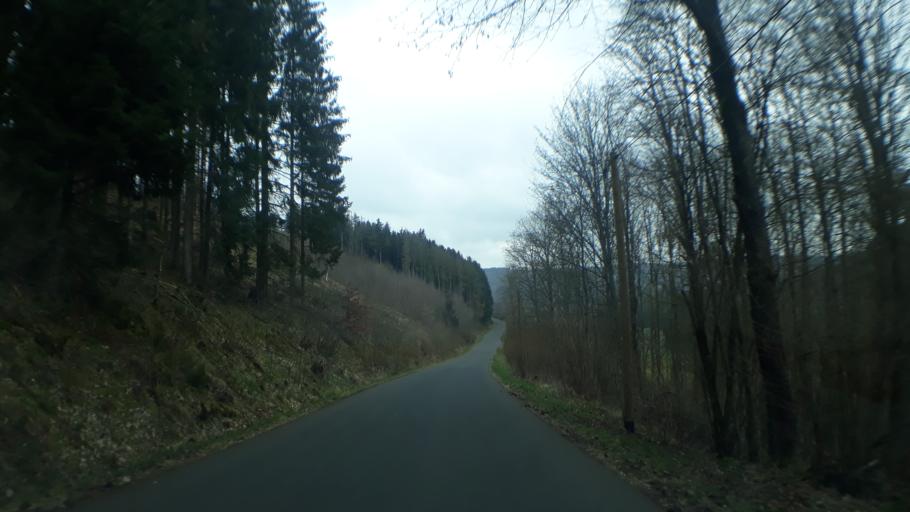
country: DE
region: North Rhine-Westphalia
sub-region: Regierungsbezirk Koln
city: Schleiden
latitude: 50.5407
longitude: 6.5017
